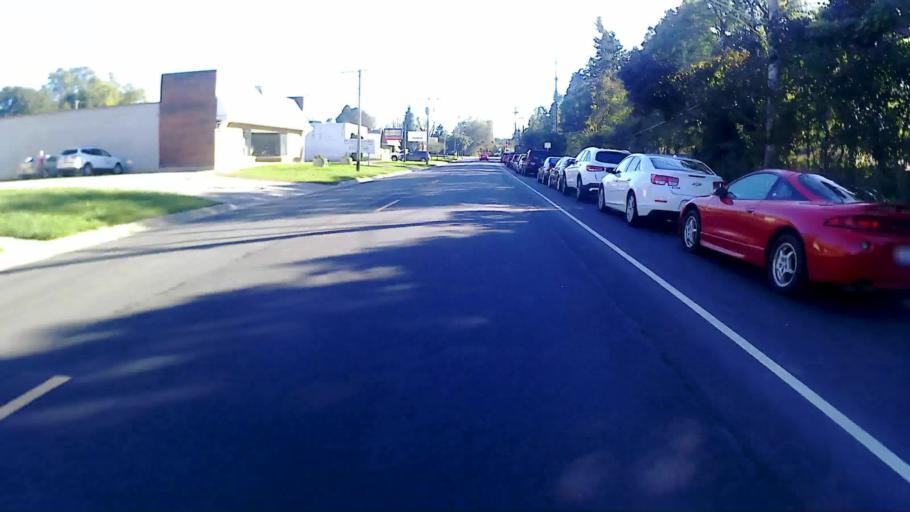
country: US
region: Illinois
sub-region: DuPage County
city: Wheaton
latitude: 41.8606
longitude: -88.1162
